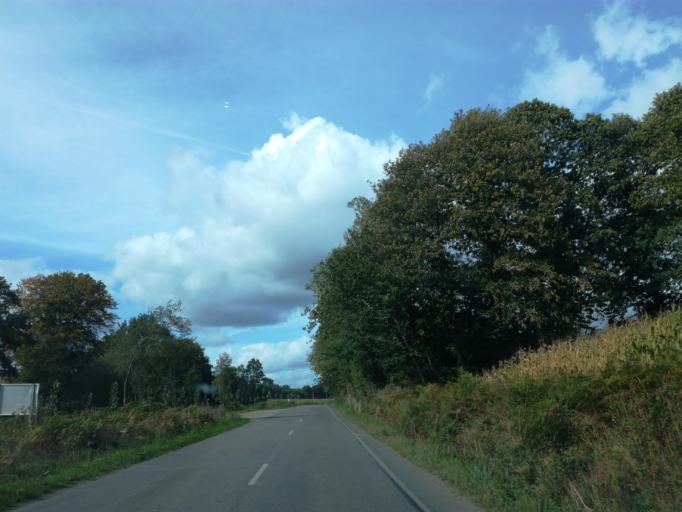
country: FR
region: Brittany
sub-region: Departement du Morbihan
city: Rohan
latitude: 48.0777
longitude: -2.7583
